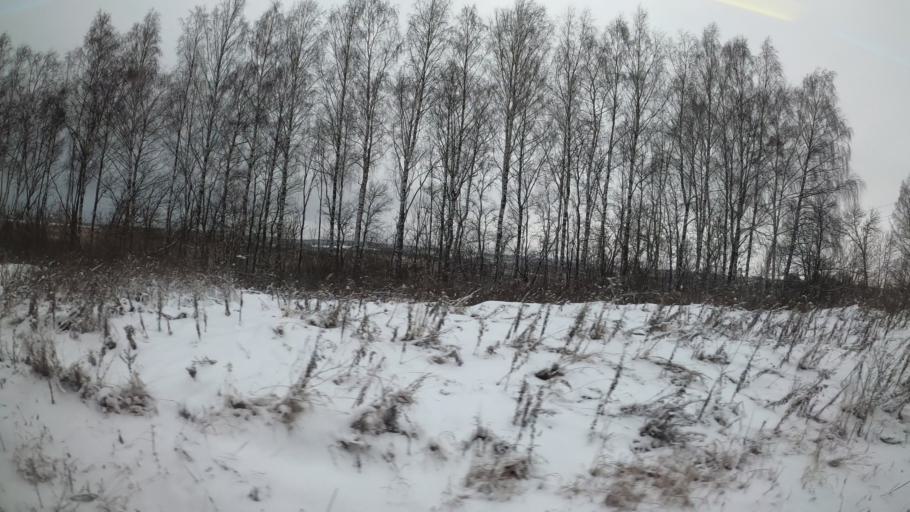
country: RU
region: Jaroslavl
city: Pereslavl'-Zalesskiy
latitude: 56.6804
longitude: 38.9190
